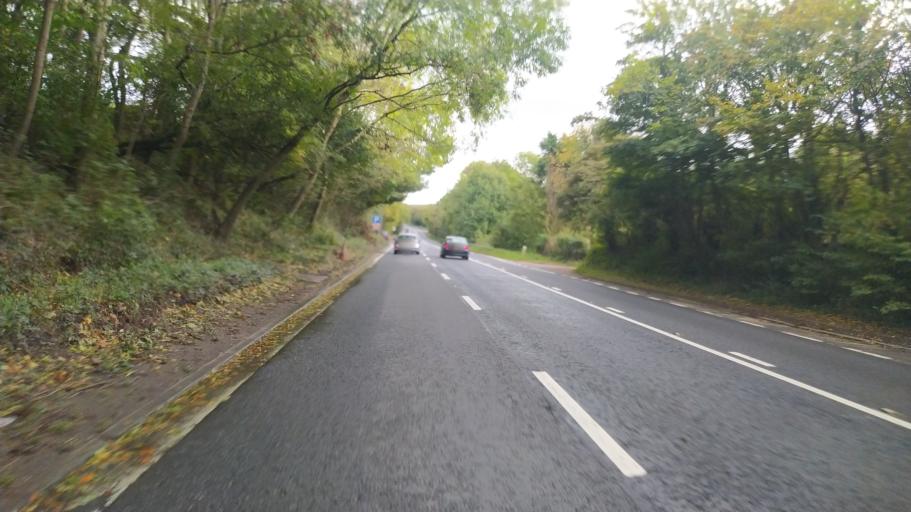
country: GB
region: England
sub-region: Dorset
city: Bridport
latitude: 50.7339
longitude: -2.7239
